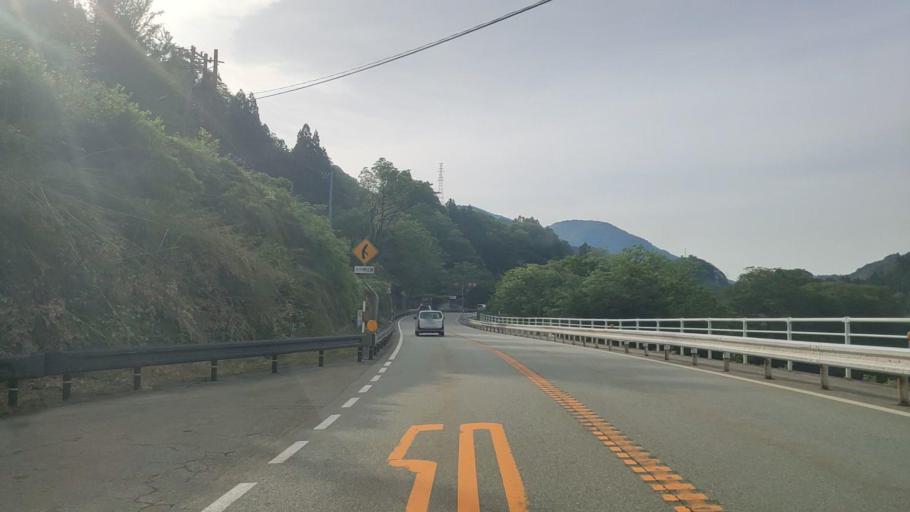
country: JP
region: Toyama
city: Yatsuomachi-higashikumisaka
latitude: 36.4548
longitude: 137.2529
